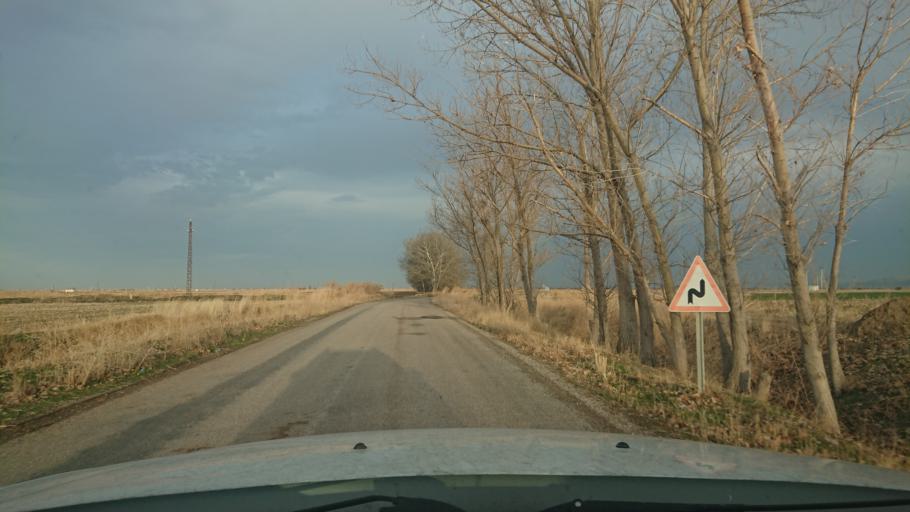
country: TR
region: Aksaray
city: Yesilova
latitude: 38.4470
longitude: 33.8359
